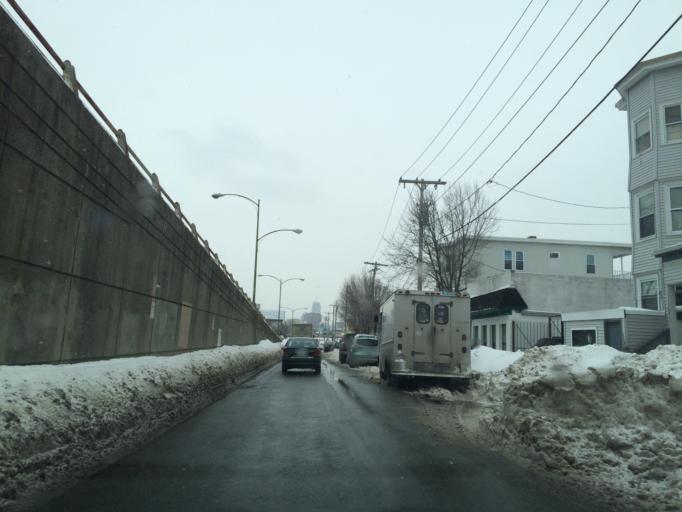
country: US
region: Massachusetts
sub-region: Middlesex County
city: Somerville
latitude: 42.3791
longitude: -71.0897
